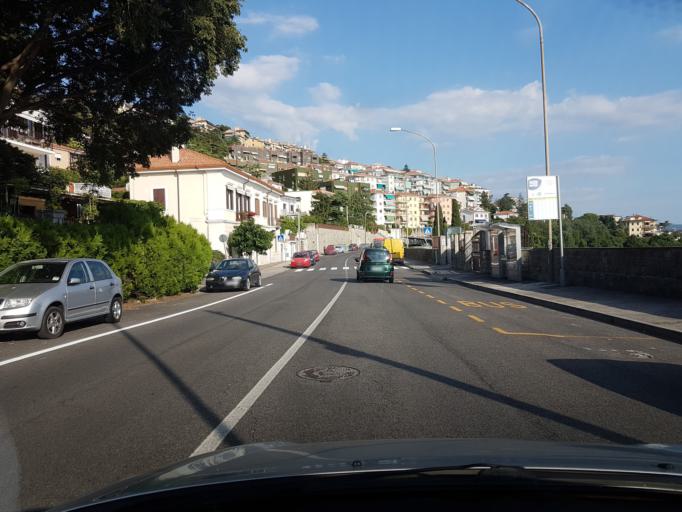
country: IT
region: Friuli Venezia Giulia
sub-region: Provincia di Trieste
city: Villa Opicina
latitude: 45.6750
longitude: 13.7573
